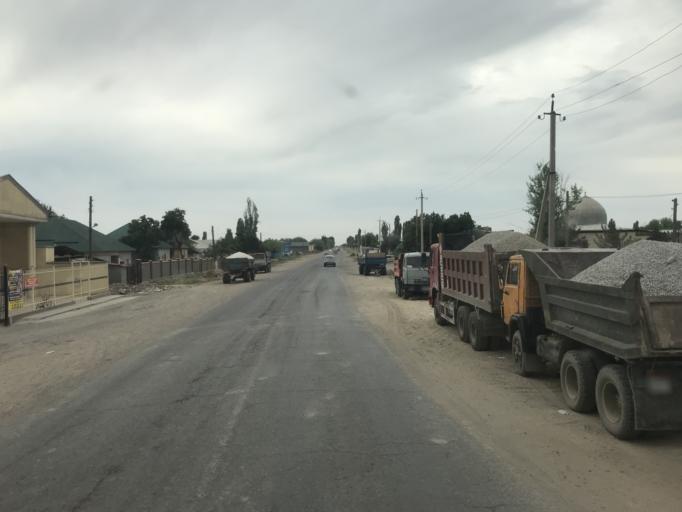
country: KZ
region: Ongtustik Qazaqstan
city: Asykata
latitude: 40.9014
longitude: 68.3584
